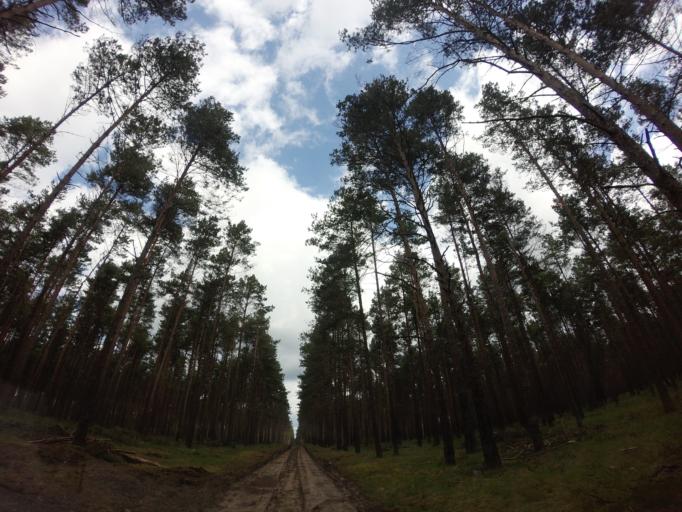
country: PL
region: West Pomeranian Voivodeship
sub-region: Powiat drawski
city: Kalisz Pomorski
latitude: 53.1839
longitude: 15.8994
